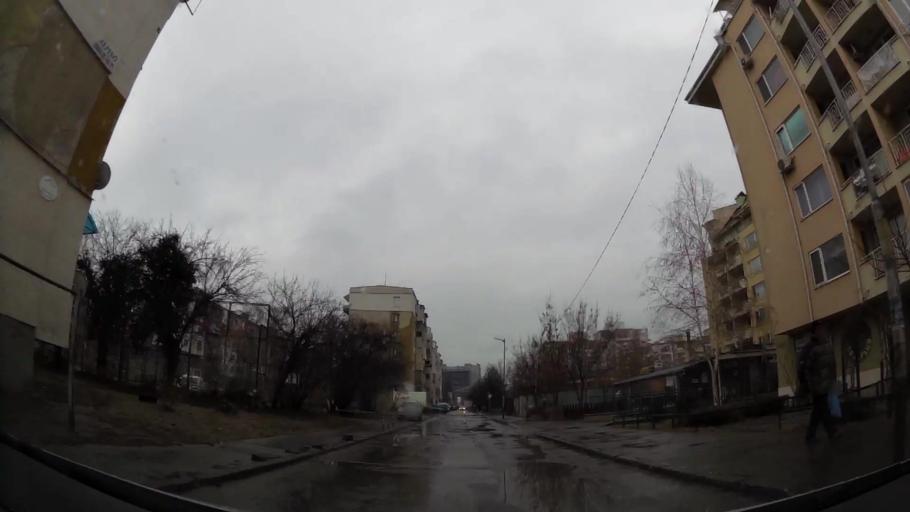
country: BG
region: Sofia-Capital
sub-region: Stolichna Obshtina
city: Sofia
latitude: 42.6640
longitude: 23.3952
